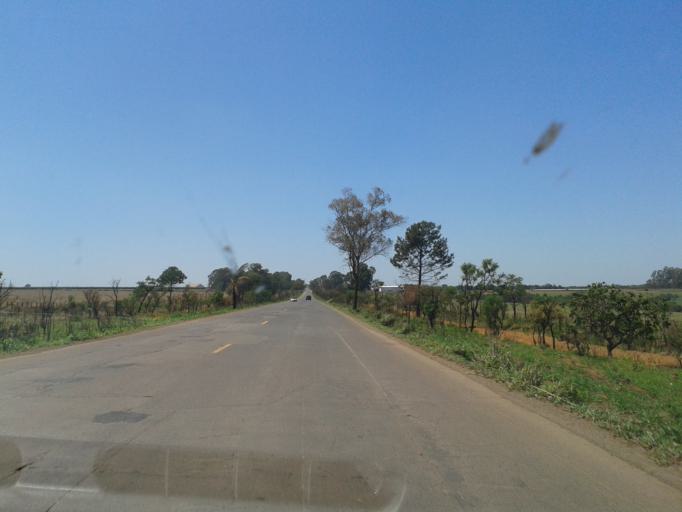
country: BR
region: Minas Gerais
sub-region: Araxa
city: Araxa
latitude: -19.4054
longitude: -47.3141
